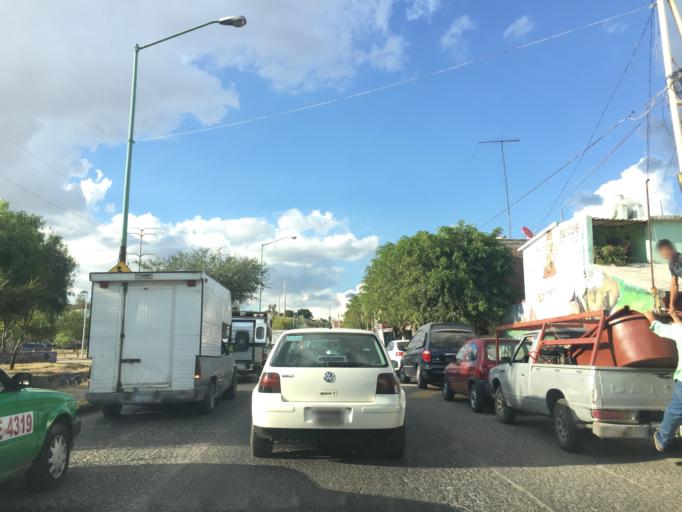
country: MX
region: Guanajuato
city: Leon
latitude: 21.1036
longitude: -101.7105
